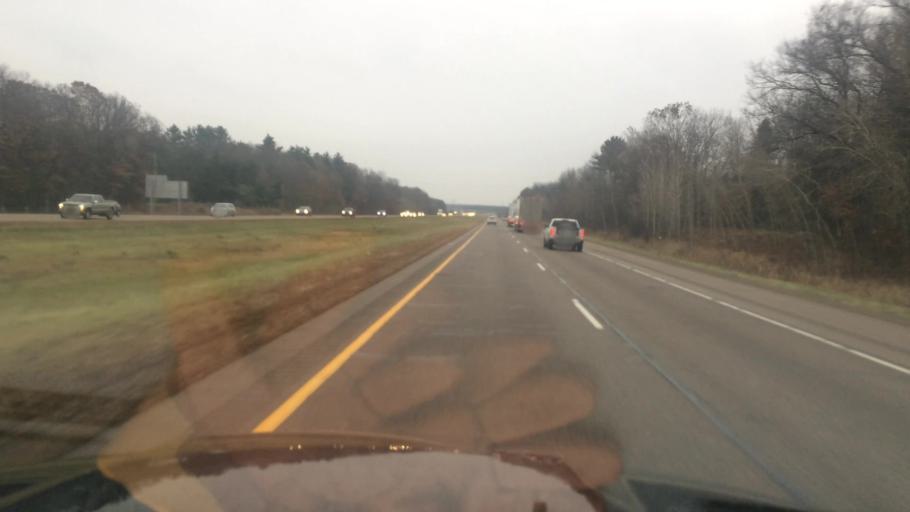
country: US
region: Wisconsin
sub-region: Portage County
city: Stevens Point
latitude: 44.5861
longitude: -89.6088
